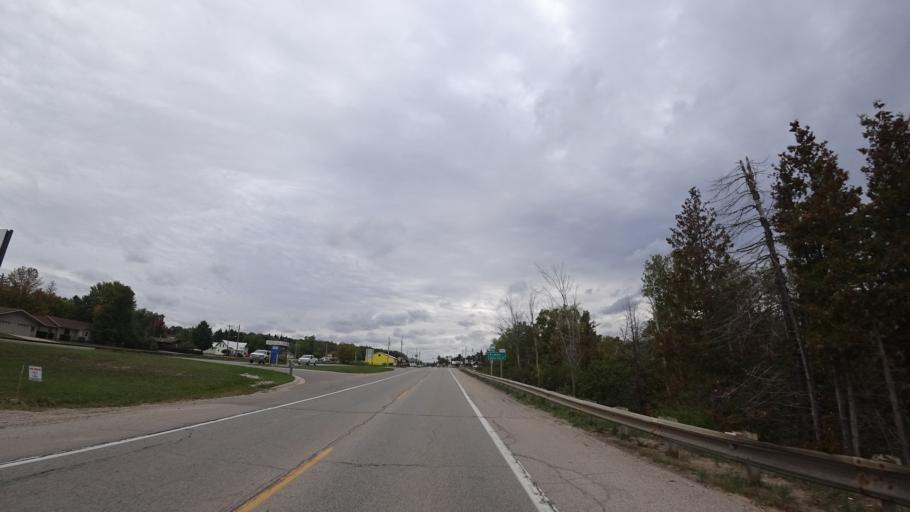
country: US
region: Michigan
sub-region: Charlevoix County
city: Boyne City
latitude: 45.1703
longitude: -84.9157
